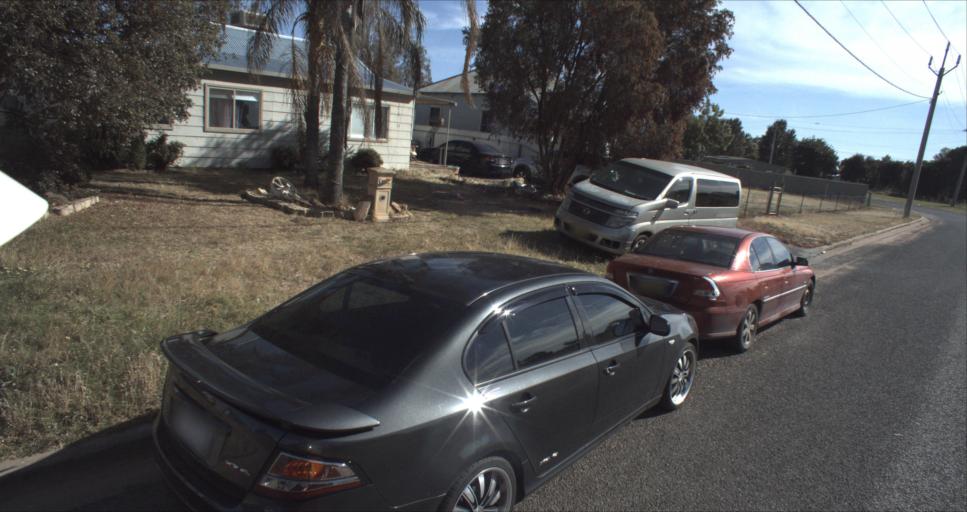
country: AU
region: New South Wales
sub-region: Leeton
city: Leeton
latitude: -34.6033
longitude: 146.4118
